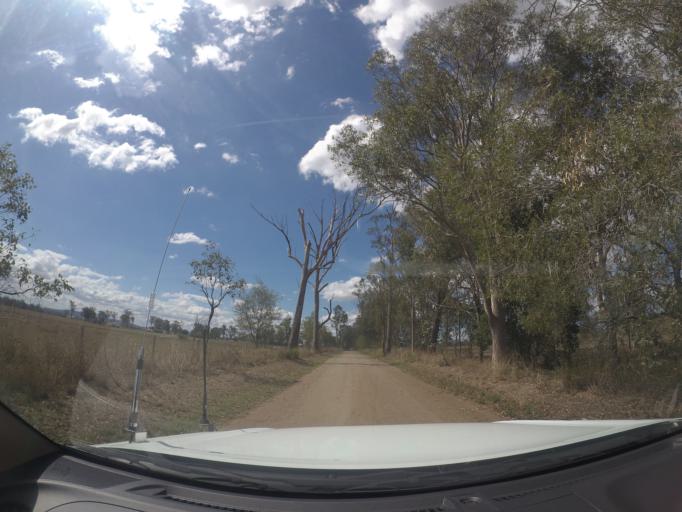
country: AU
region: Queensland
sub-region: Logan
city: Cedar Vale
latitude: -27.8891
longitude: 152.9598
